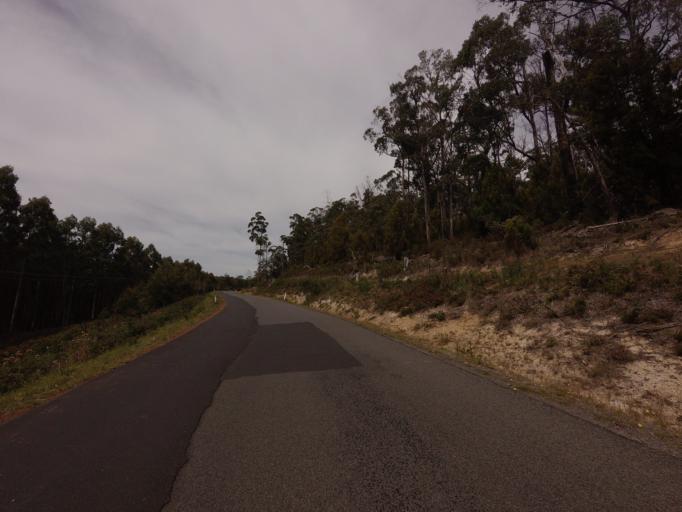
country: AU
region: Tasmania
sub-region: Sorell
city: Sorell
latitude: -42.5844
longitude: 147.5582
